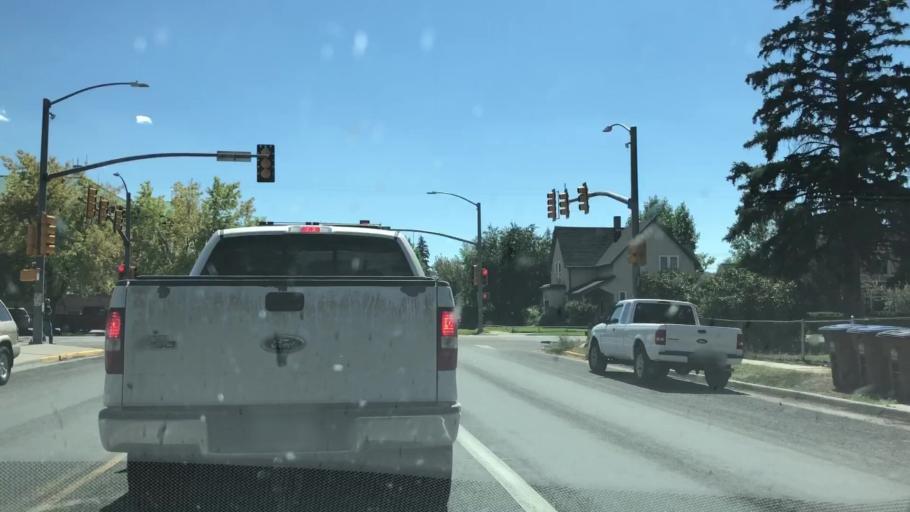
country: US
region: Wyoming
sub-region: Albany County
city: Laramie
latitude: 41.3109
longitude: -105.5857
